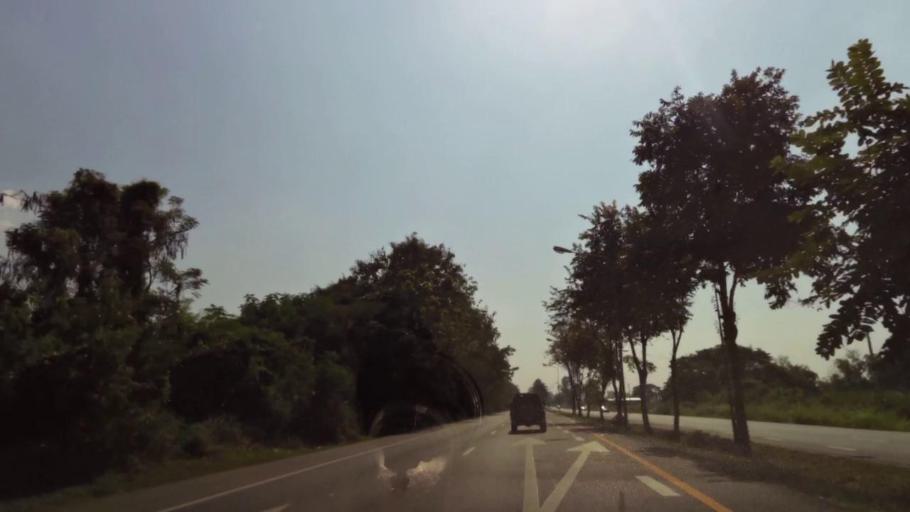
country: TH
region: Phichit
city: Bueng Na Rang
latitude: 16.0919
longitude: 100.1252
